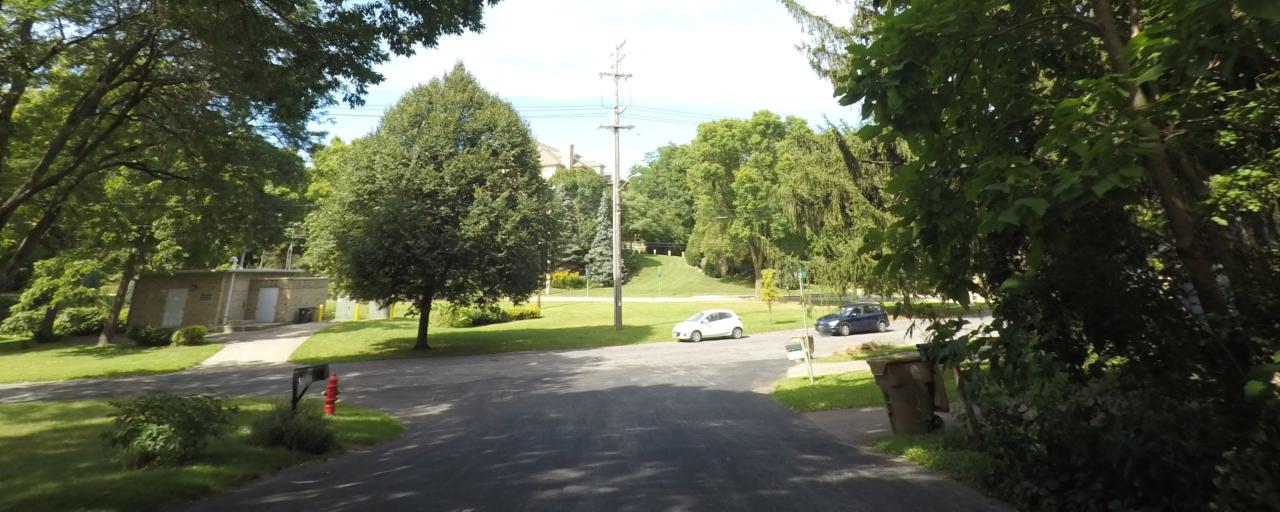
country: US
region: Wisconsin
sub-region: Dane County
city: Shorewood Hills
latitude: 43.0736
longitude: -89.4741
